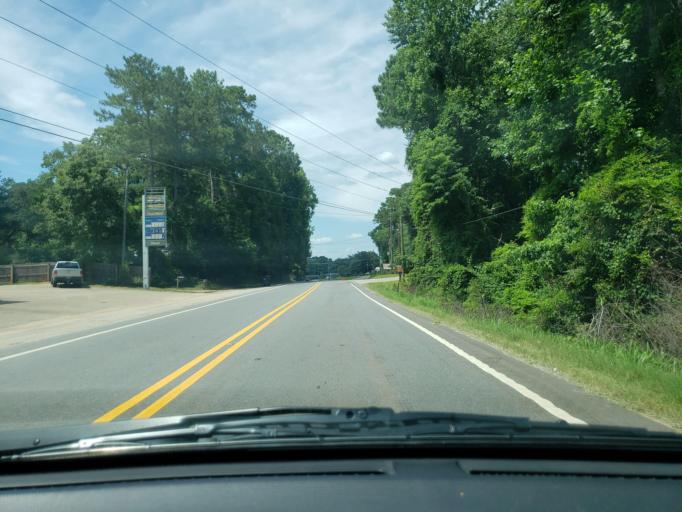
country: US
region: Alabama
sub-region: Elmore County
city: Eclectic
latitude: 32.6811
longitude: -85.9432
